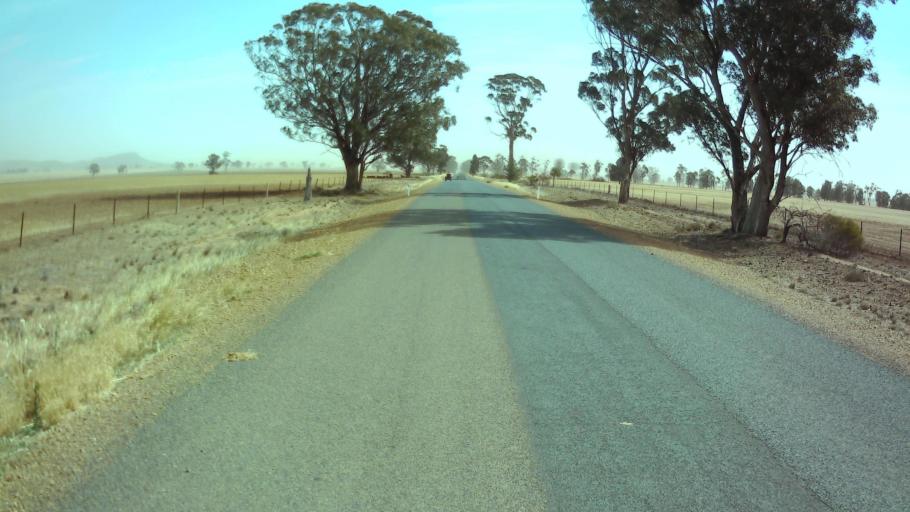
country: AU
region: New South Wales
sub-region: Weddin
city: Grenfell
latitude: -33.7698
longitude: 147.9871
